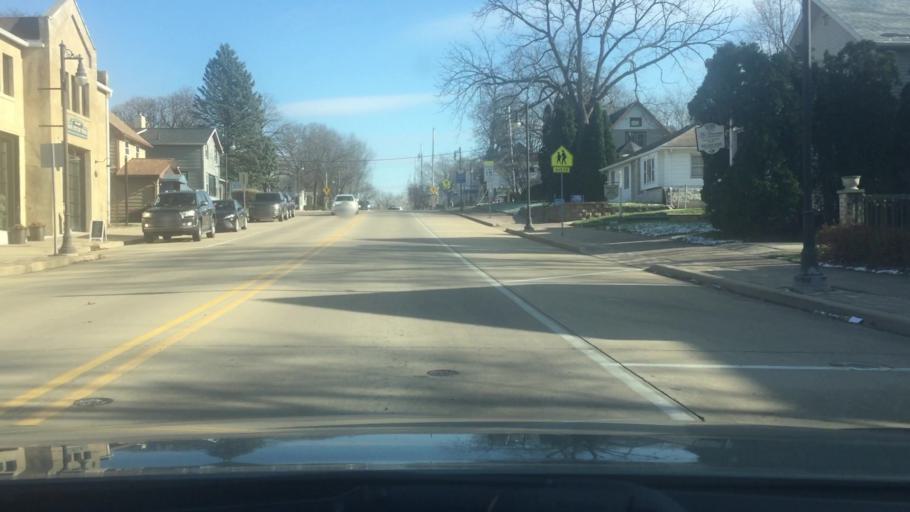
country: US
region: Wisconsin
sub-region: Jefferson County
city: Cambridge
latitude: 43.0035
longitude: -89.0163
